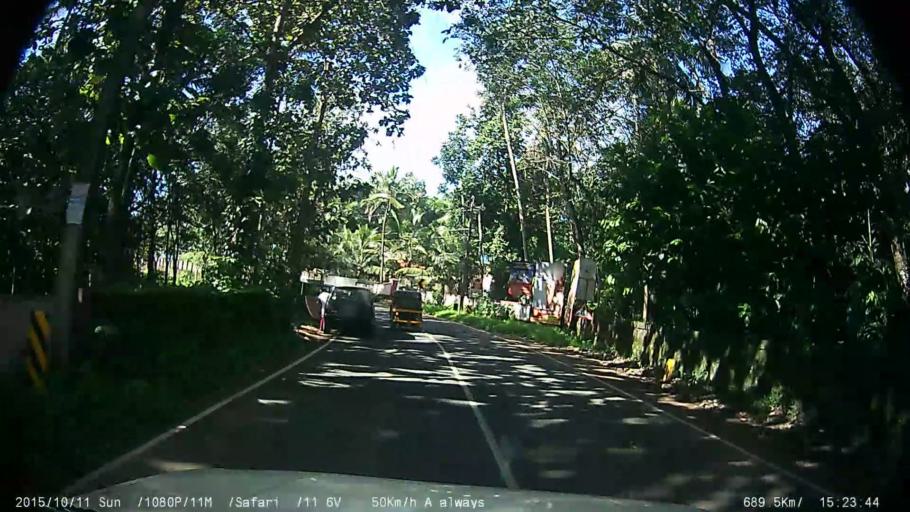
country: IN
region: Kerala
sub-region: Kottayam
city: Changanacheri
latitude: 9.4675
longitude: 76.5785
